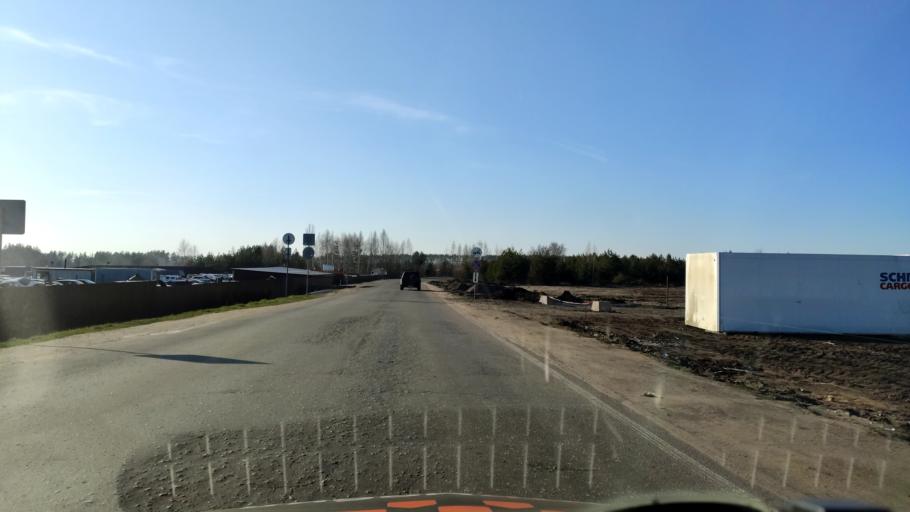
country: RU
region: Voronezj
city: Podgornoye
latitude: 51.8272
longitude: 39.2100
